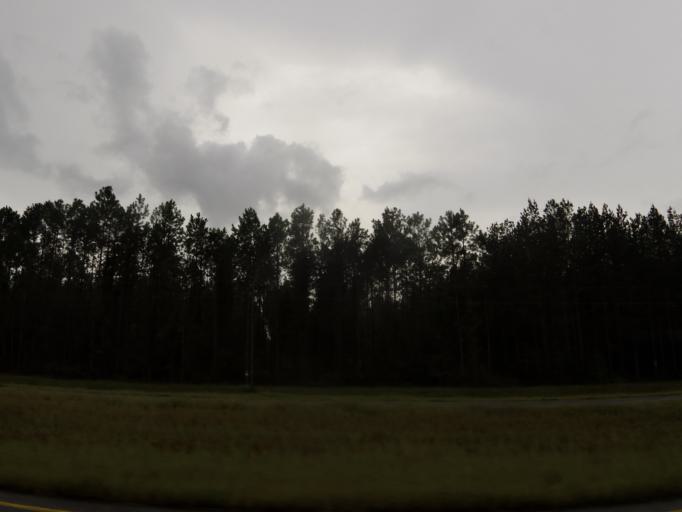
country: US
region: Georgia
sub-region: Wayne County
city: Jesup
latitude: 31.4511
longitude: -81.6983
